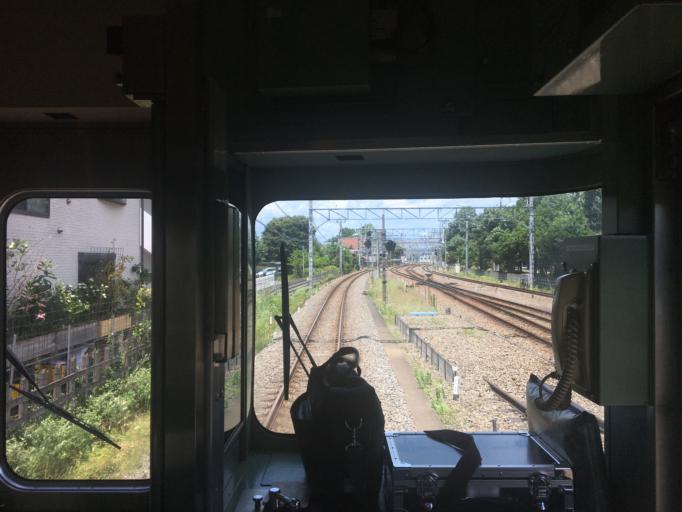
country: JP
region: Tokyo
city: Higashimurayama-shi
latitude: 35.7375
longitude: 139.4871
